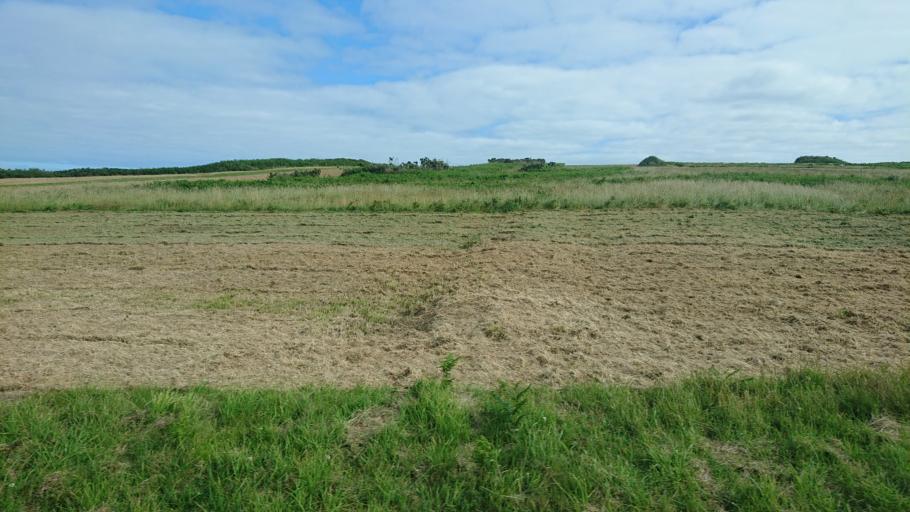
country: FR
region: Brittany
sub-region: Departement du Finistere
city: Porspoder
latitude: 48.4683
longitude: -5.0602
